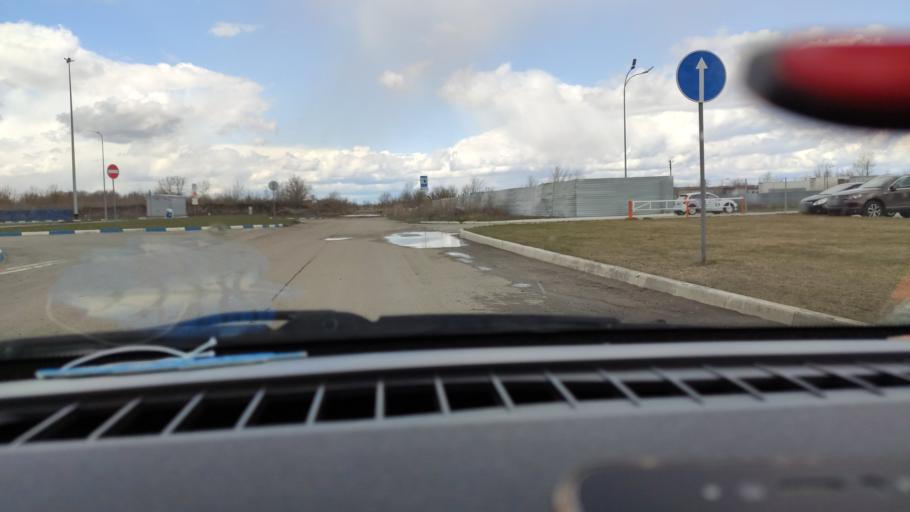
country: RU
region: Samara
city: Tol'yatti
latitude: 53.5391
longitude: 49.2610
